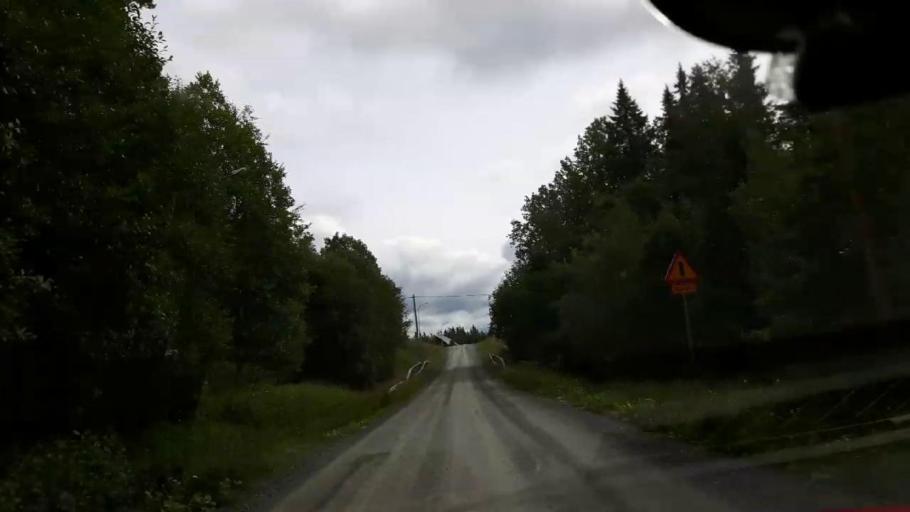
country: SE
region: Jaemtland
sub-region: Krokoms Kommun
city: Valla
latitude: 63.6714
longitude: 13.9531
